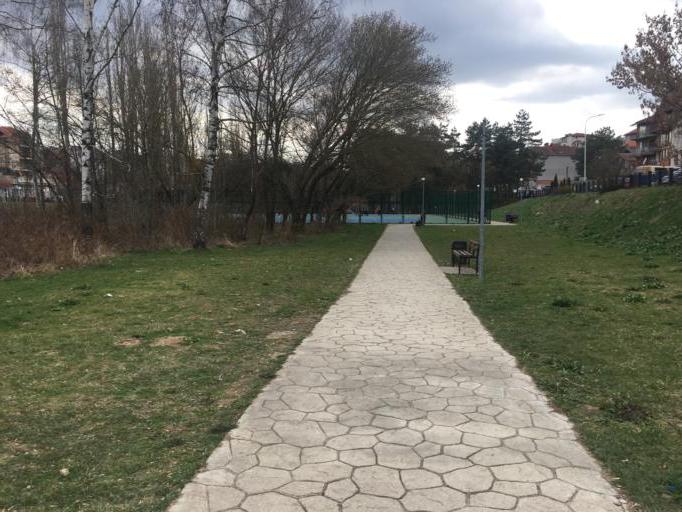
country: XK
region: Pristina
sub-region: Komuna e Prishtines
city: Pristina
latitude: 42.6677
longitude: 21.1881
